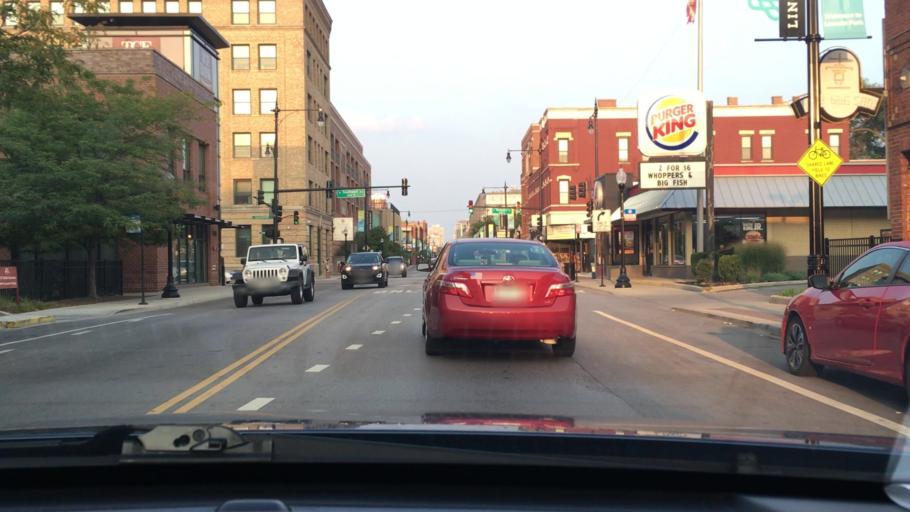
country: US
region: Illinois
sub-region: Cook County
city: Chicago
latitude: 41.9252
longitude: -87.6640
